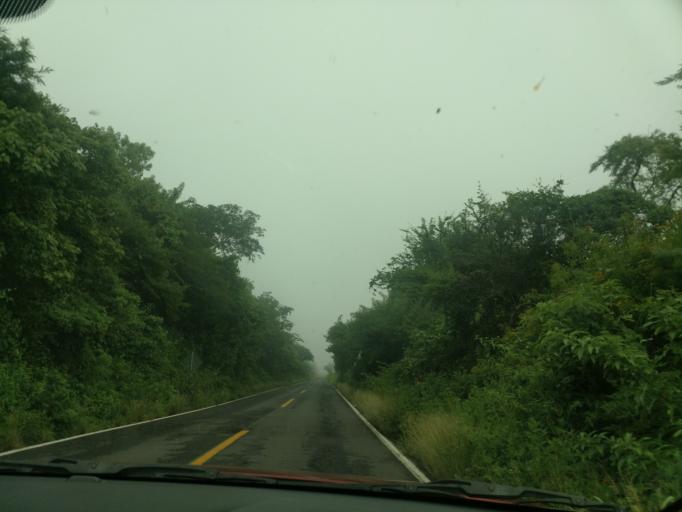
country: MX
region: Jalisco
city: Ameca
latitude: 20.5452
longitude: -104.1486
